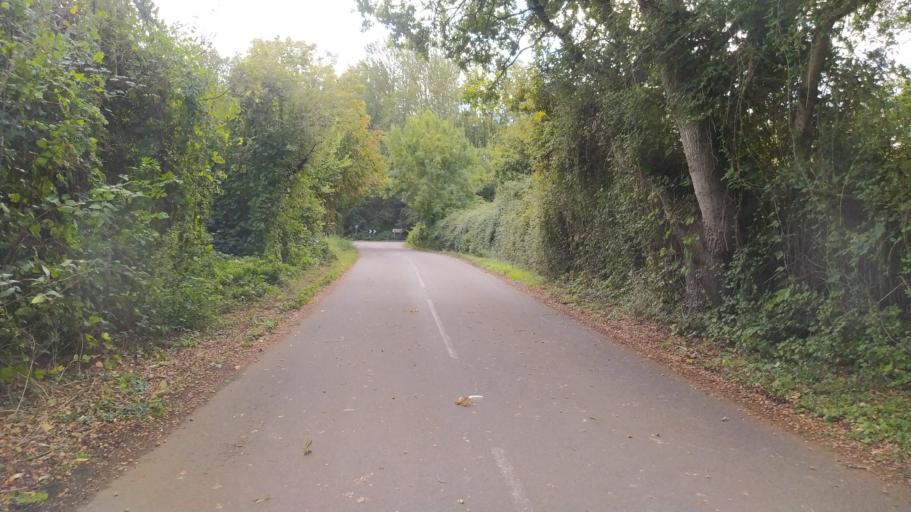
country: GB
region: England
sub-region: West Berkshire
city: Calcot
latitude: 51.4251
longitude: -1.0074
